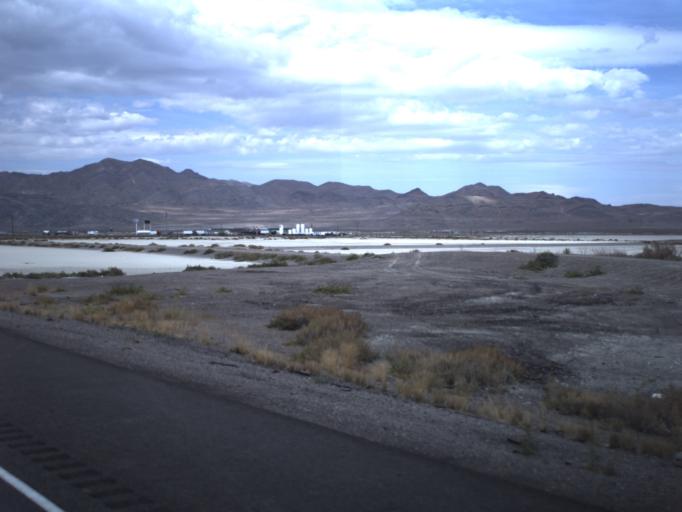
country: US
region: Utah
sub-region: Tooele County
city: Wendover
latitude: 40.7416
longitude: -113.9612
